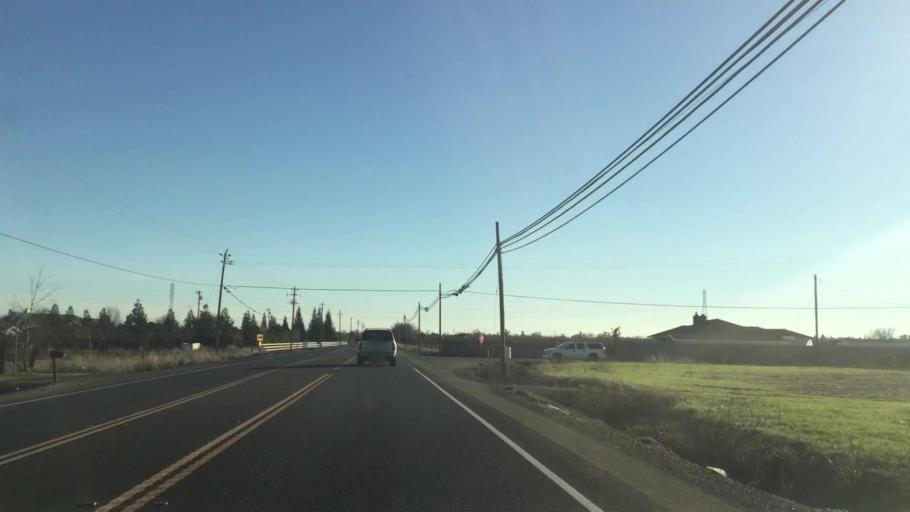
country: US
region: California
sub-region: Yuba County
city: Marysville
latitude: 39.1819
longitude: -121.5926
